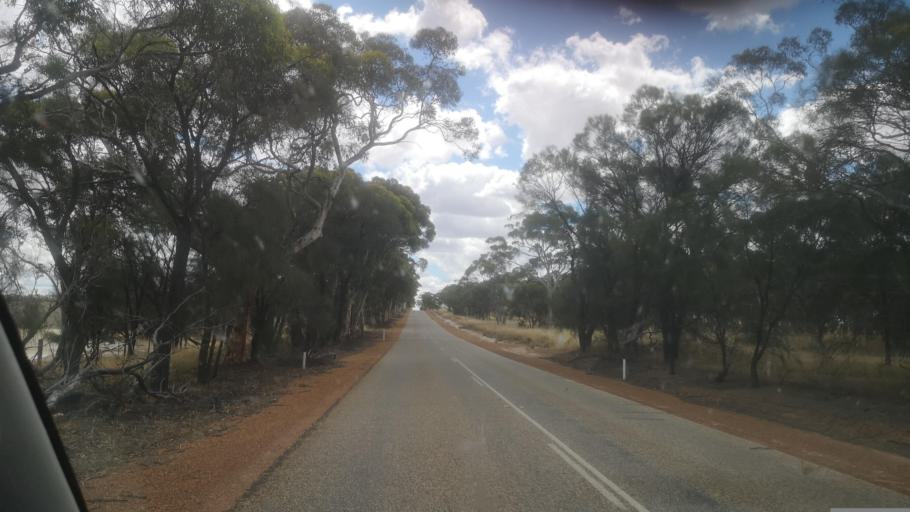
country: AU
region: Western Australia
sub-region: Beverley
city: Beverley
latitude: -31.9899
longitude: 117.1136
